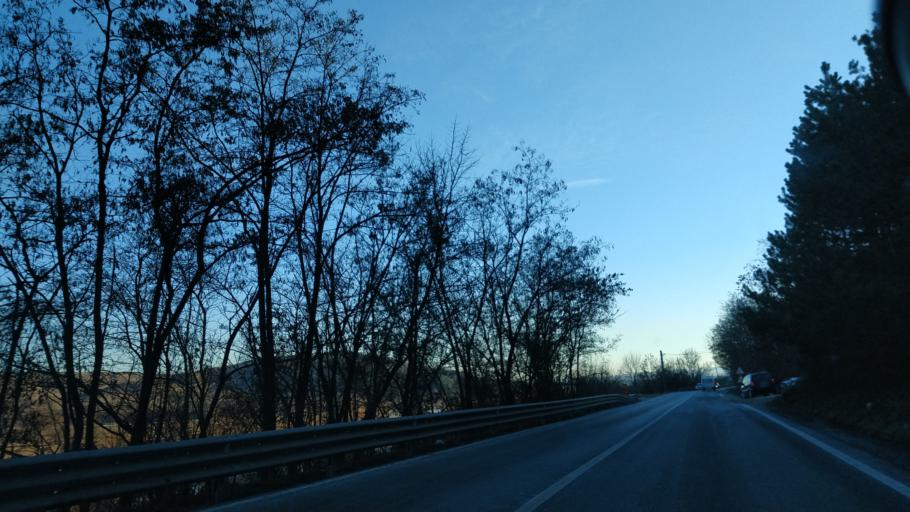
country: RO
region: Bacau
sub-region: Comuna Helegiu
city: Bratila
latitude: 46.3051
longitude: 26.7521
